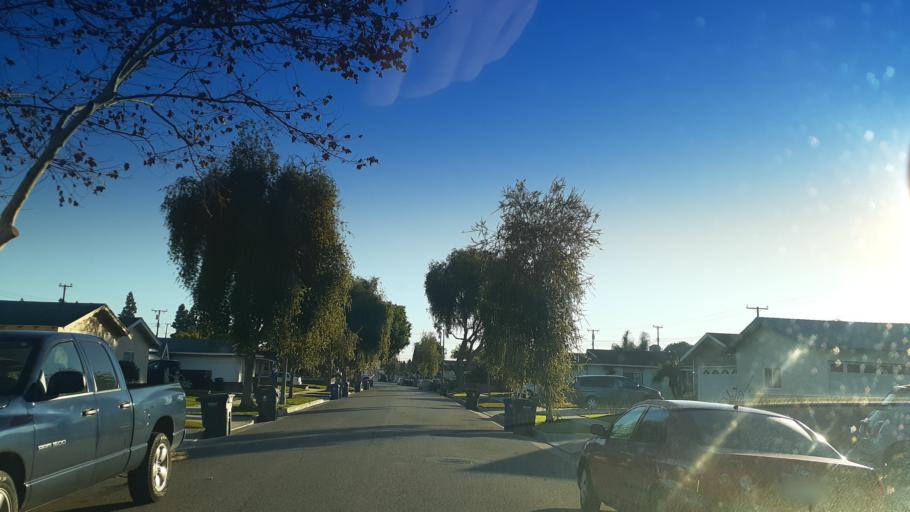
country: US
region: California
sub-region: Los Angeles County
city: Hawaiian Gardens
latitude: 33.8441
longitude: -118.0890
